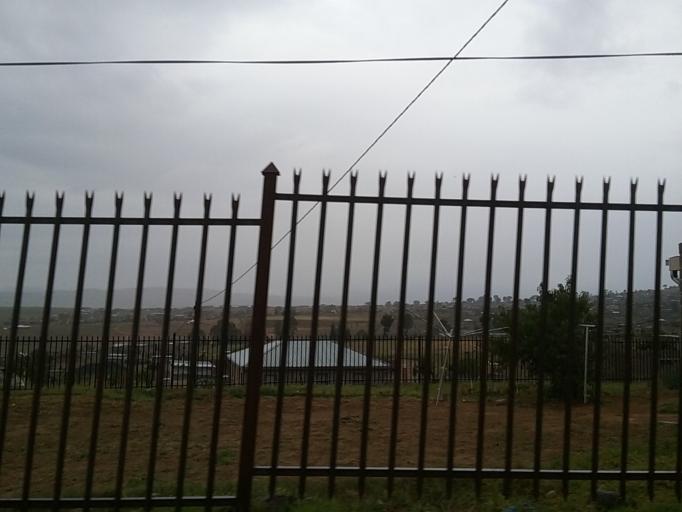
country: LS
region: Berea
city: Teyateyaneng
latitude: -29.1269
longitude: 27.7443
